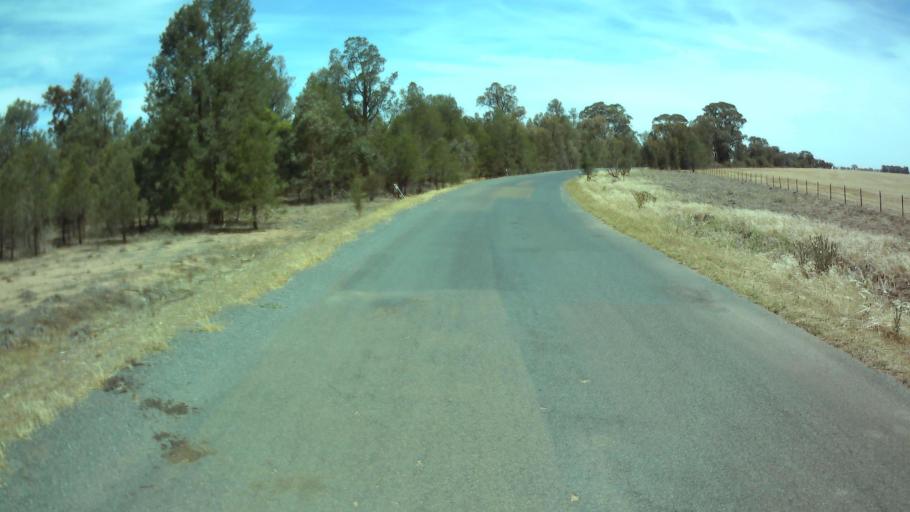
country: AU
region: New South Wales
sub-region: Weddin
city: Grenfell
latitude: -33.9447
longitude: 147.7787
